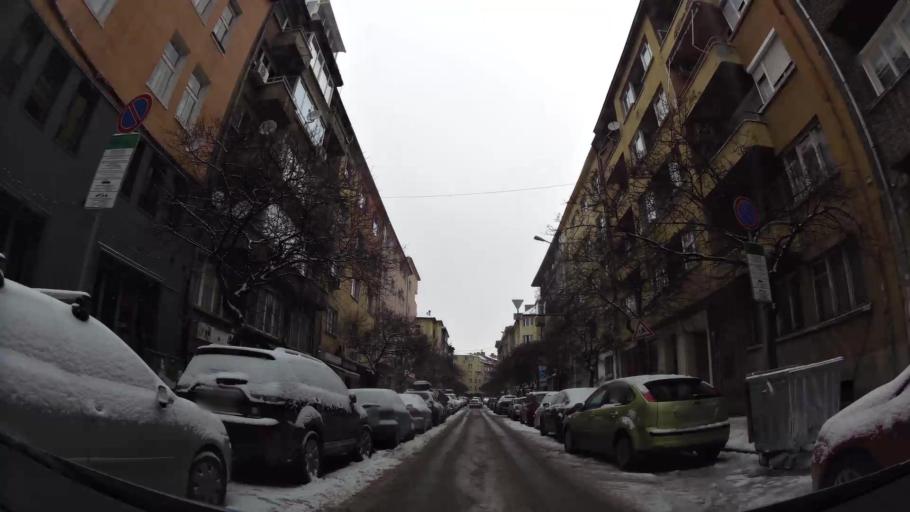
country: BG
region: Sofia-Capital
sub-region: Stolichna Obshtina
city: Sofia
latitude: 42.6847
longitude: 23.3234
